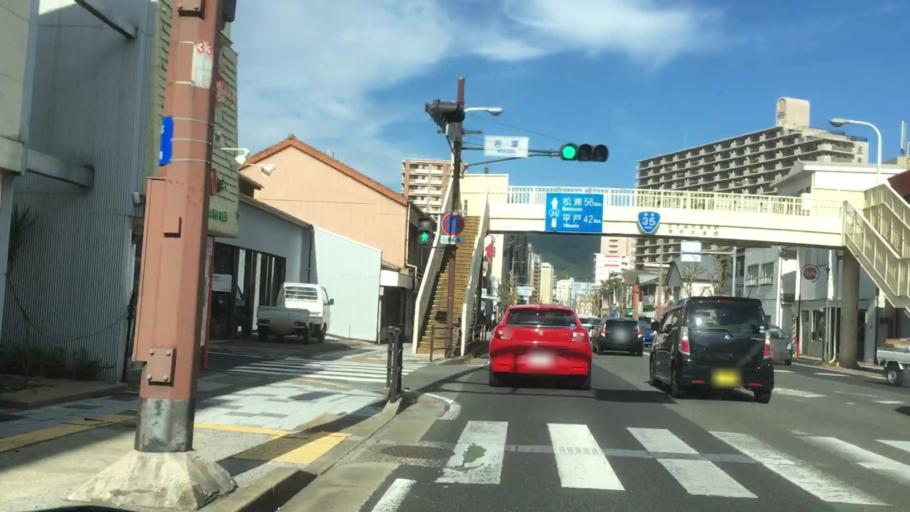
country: JP
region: Nagasaki
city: Sasebo
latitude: 33.1609
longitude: 129.7313
